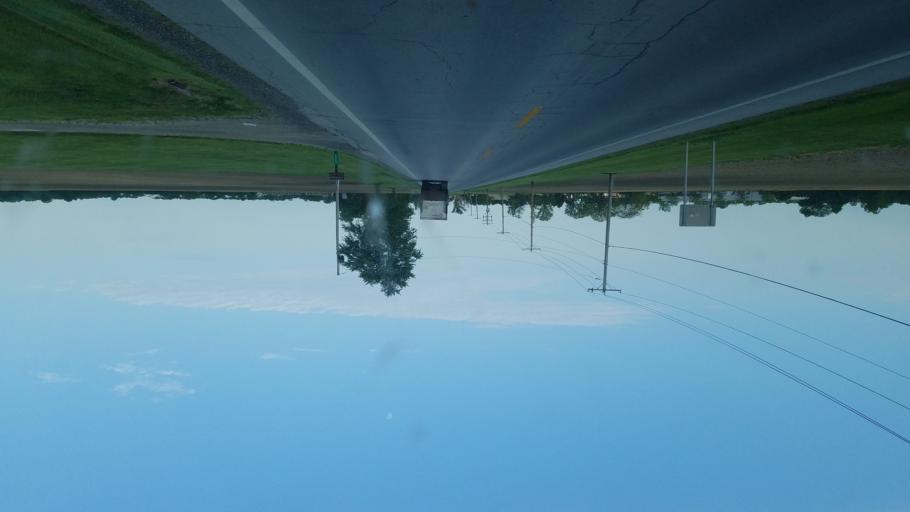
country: US
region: Ohio
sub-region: Fayette County
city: Washington Court House
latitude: 39.5584
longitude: -83.4148
